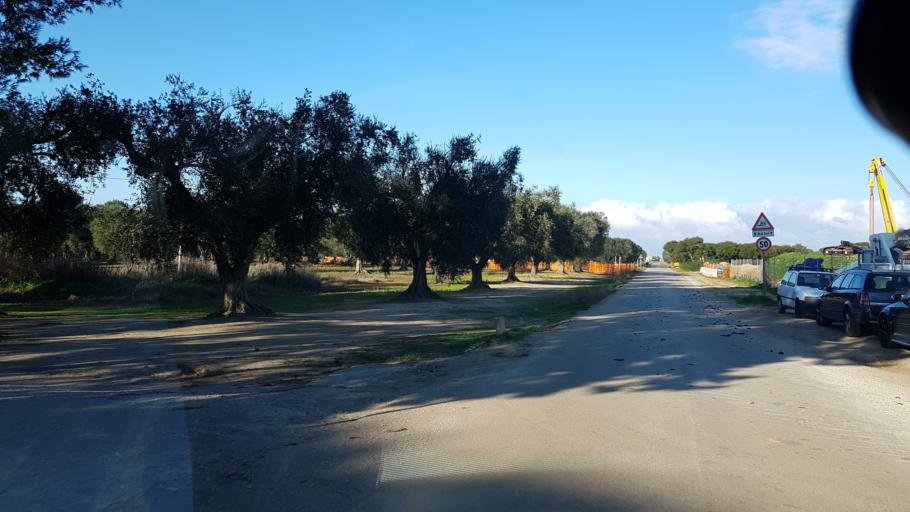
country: IT
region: Apulia
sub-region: Provincia di Brindisi
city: Tuturano
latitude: 40.5680
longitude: 17.8987
